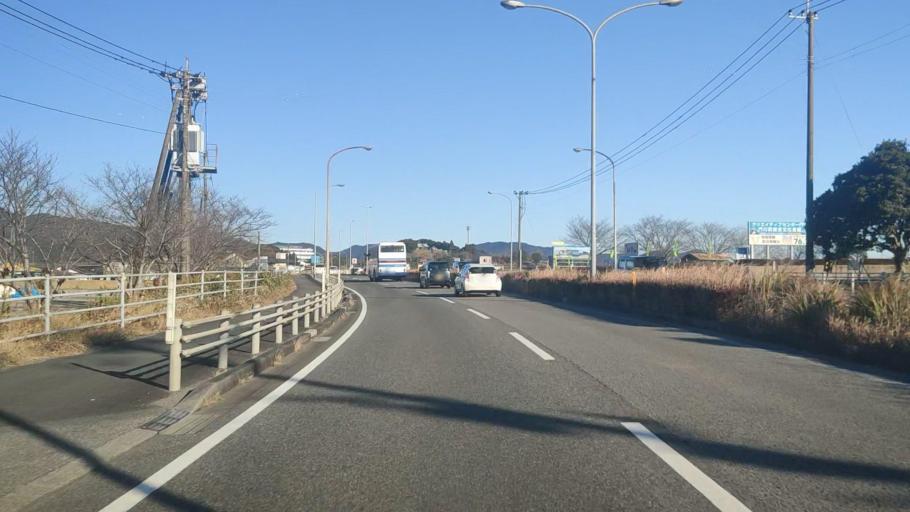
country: JP
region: Miyazaki
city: Nobeoka
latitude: 32.4629
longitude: 131.6488
